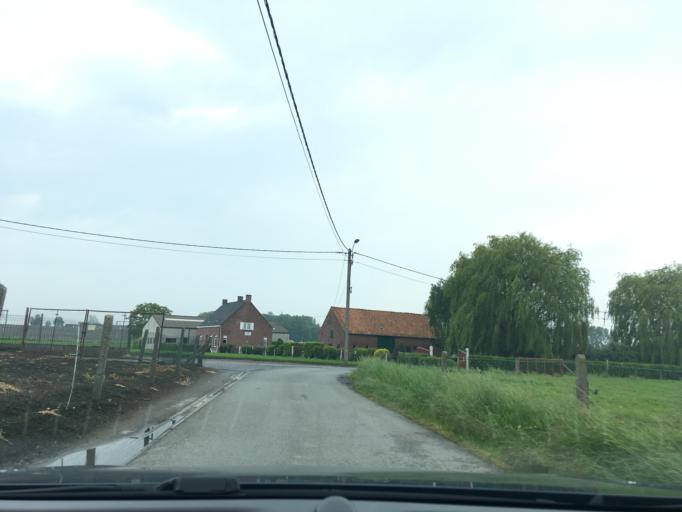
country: BE
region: Flanders
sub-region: Provincie West-Vlaanderen
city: Lichtervelde
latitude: 51.0047
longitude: 3.1235
